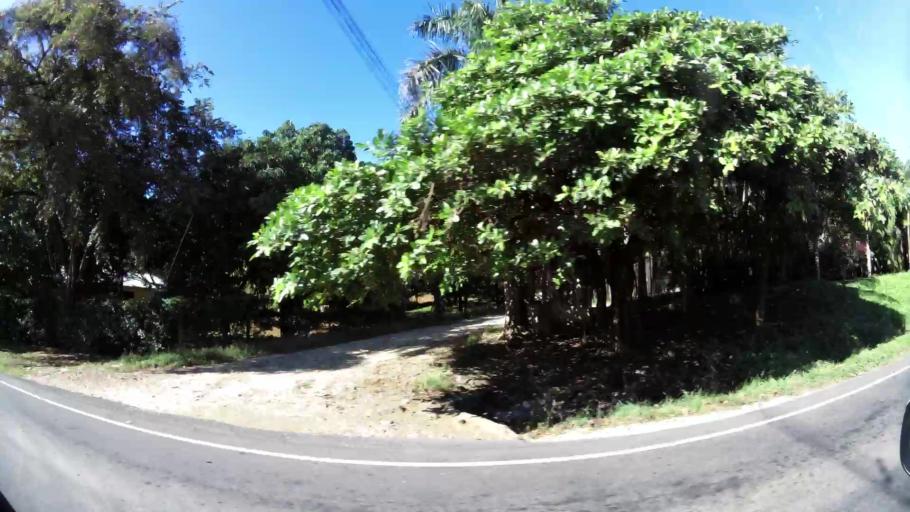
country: CR
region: Guanacaste
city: Belen
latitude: 10.3606
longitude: -85.7505
